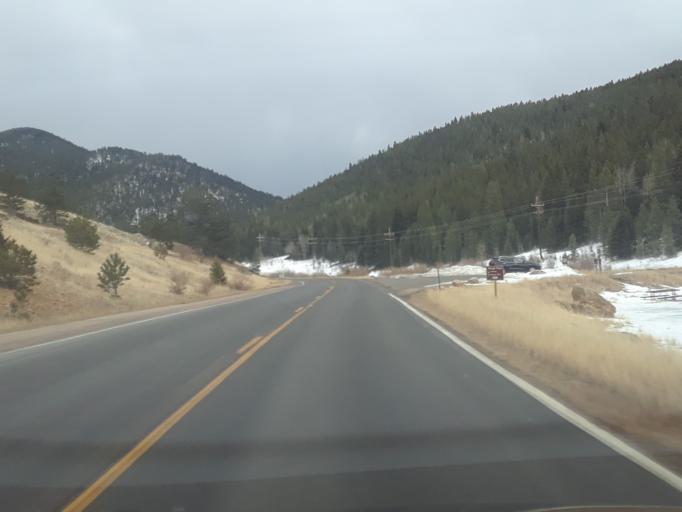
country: US
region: Colorado
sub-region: Boulder County
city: Coal Creek
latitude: 39.8318
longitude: -105.4230
